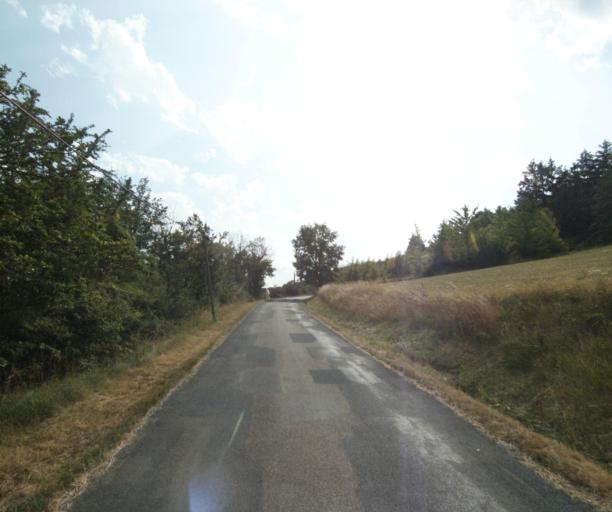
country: FR
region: Rhone-Alpes
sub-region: Departement du Rhone
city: Bully
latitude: 45.8561
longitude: 4.5925
